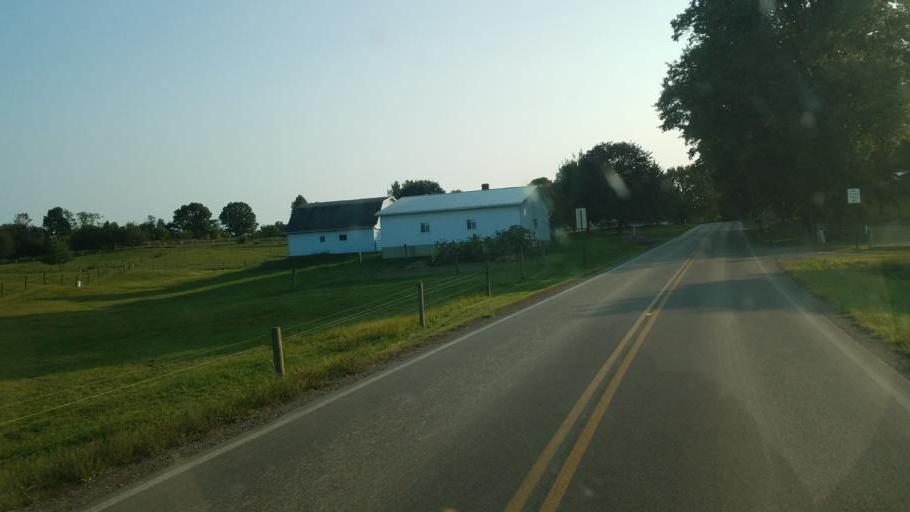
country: US
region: Ohio
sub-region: Wayne County
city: Apple Creek
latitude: 40.7276
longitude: -81.8200
